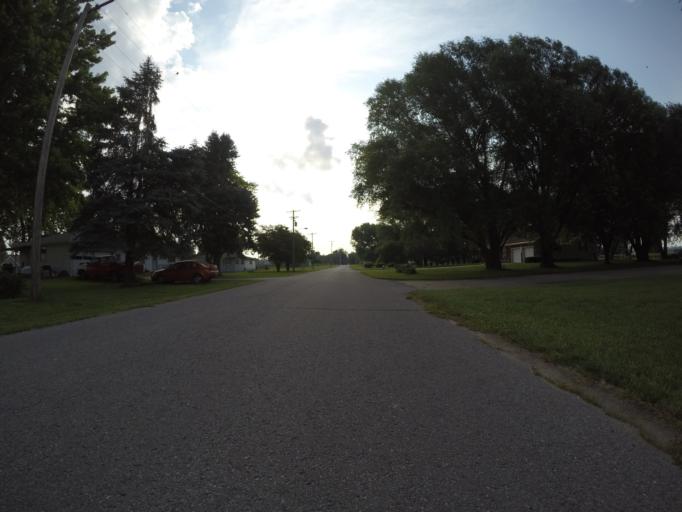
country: US
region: Kansas
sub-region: Doniphan County
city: Elwood
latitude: 39.7518
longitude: -94.8815
